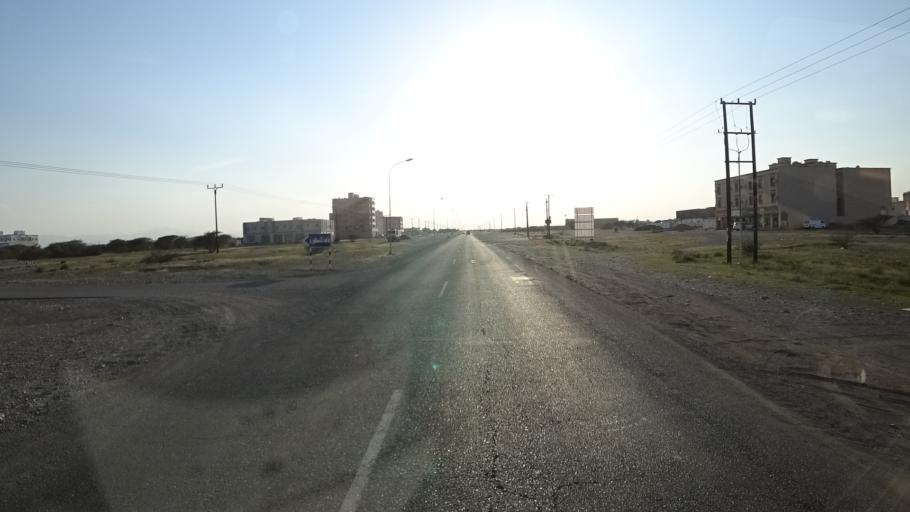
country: OM
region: Al Batinah
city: Al Khaburah
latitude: 23.9517
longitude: 57.0592
